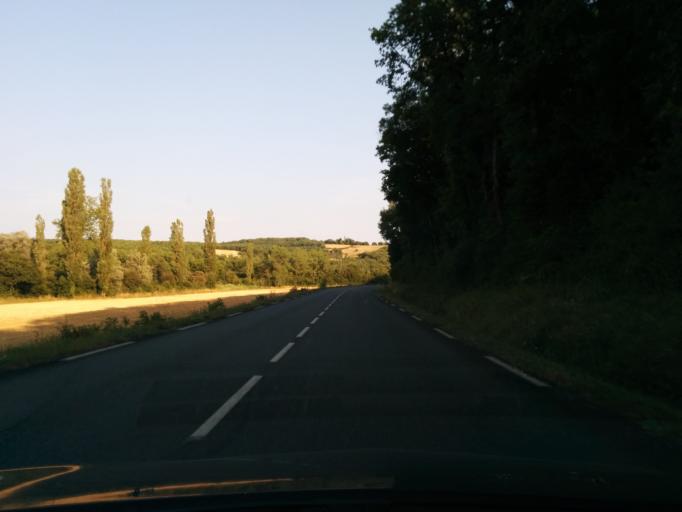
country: FR
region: Midi-Pyrenees
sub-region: Departement du Lot
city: Le Vigan
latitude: 44.6952
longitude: 1.4823
